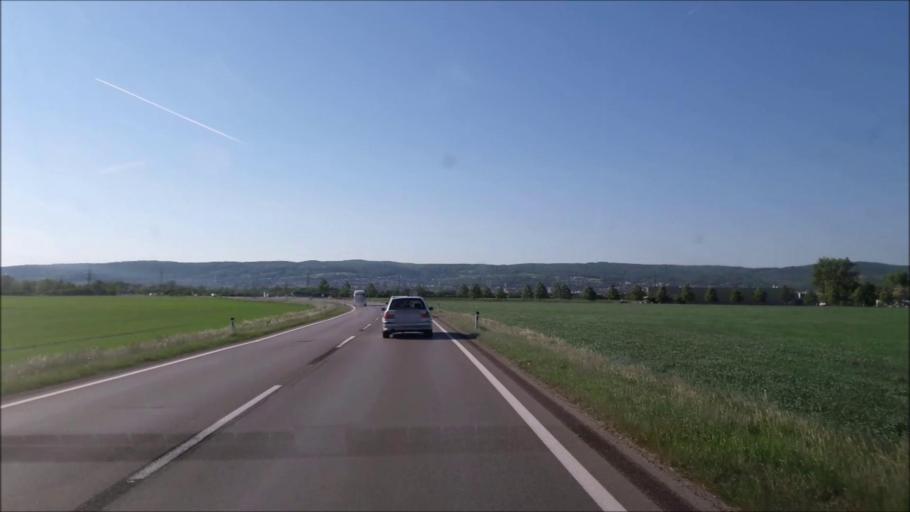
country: AT
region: Burgenland
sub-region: Eisenstadt-Umgebung
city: Trausdorf an der Wulka
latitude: 47.8178
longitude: 16.5453
